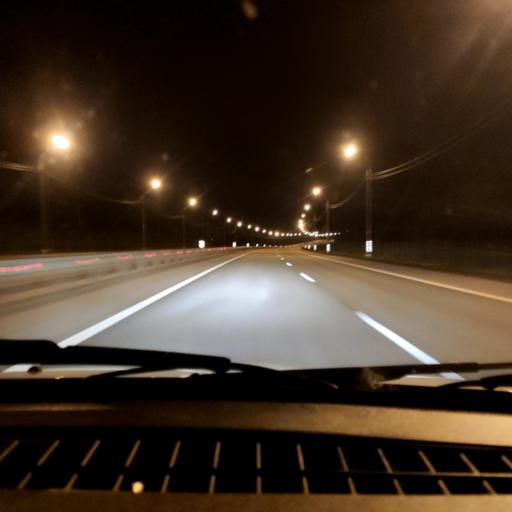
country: RU
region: Lipetsk
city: Zadonsk
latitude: 52.3389
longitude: 38.9682
